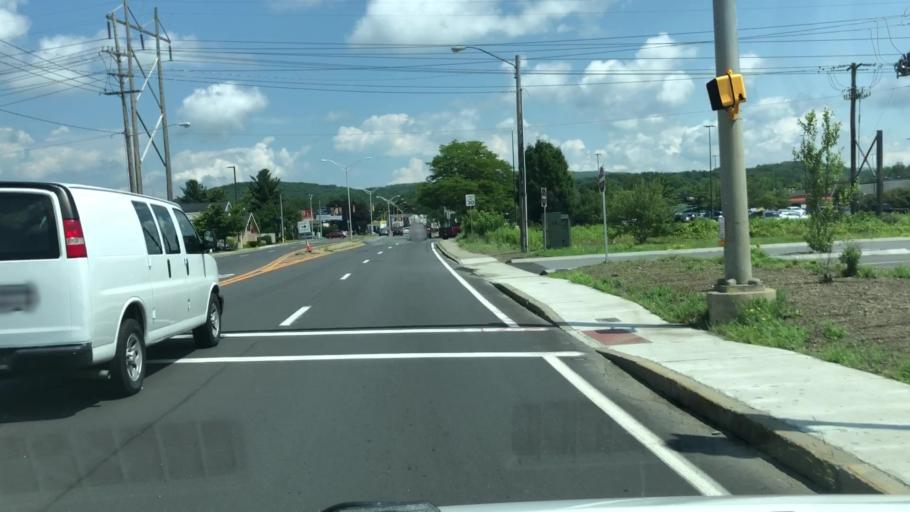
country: US
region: Massachusetts
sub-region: Berkshire County
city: Dalton
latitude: 42.4650
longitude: -73.2055
